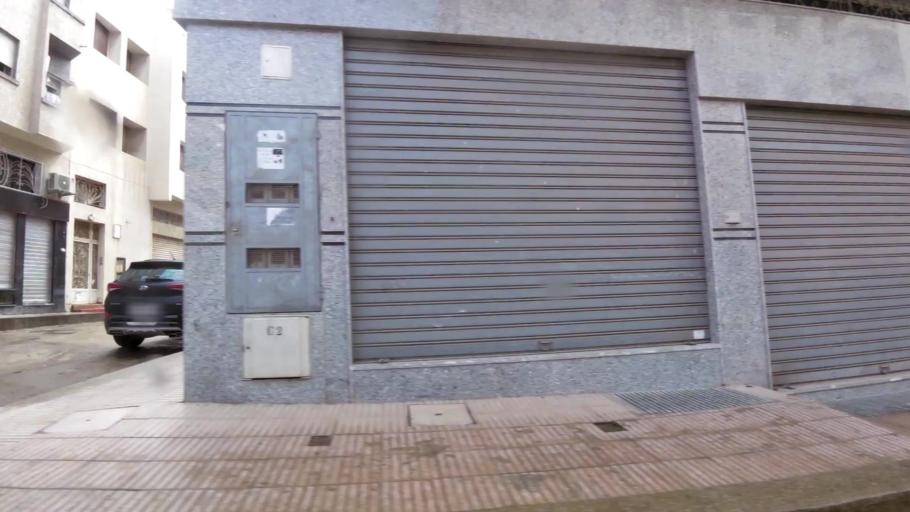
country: MA
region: Grand Casablanca
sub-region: Casablanca
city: Casablanca
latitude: 33.5308
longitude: -7.6493
